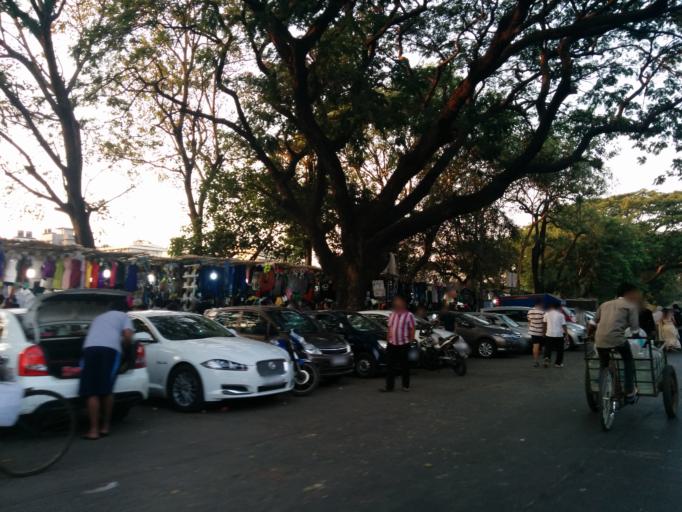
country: IN
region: Maharashtra
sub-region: Raigarh
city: Uran
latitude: 18.9363
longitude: 72.8305
